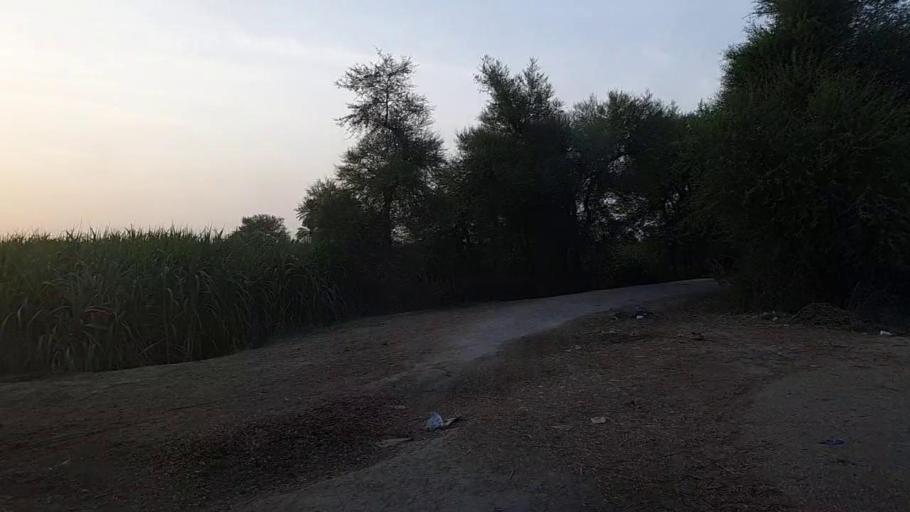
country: PK
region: Sindh
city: Ubauro
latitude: 28.2899
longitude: 69.7997
